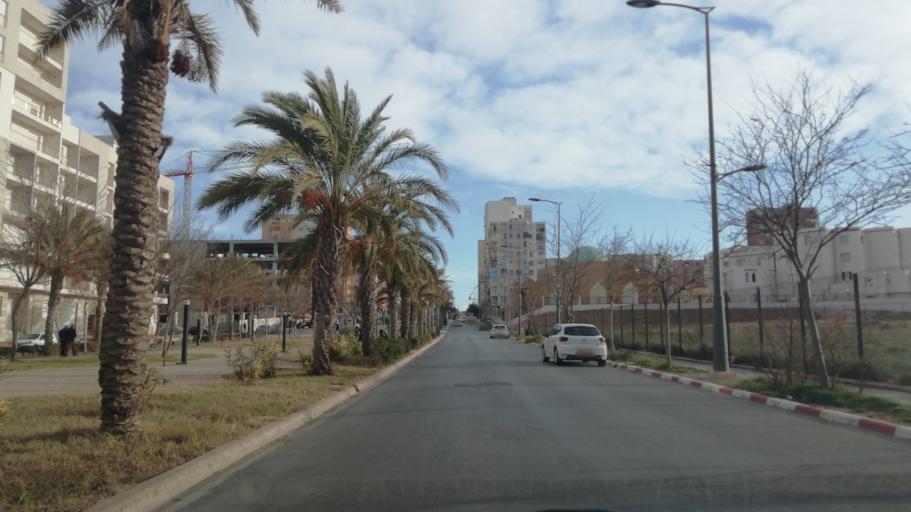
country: DZ
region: Oran
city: Bir el Djir
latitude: 35.7245
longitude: -0.5936
